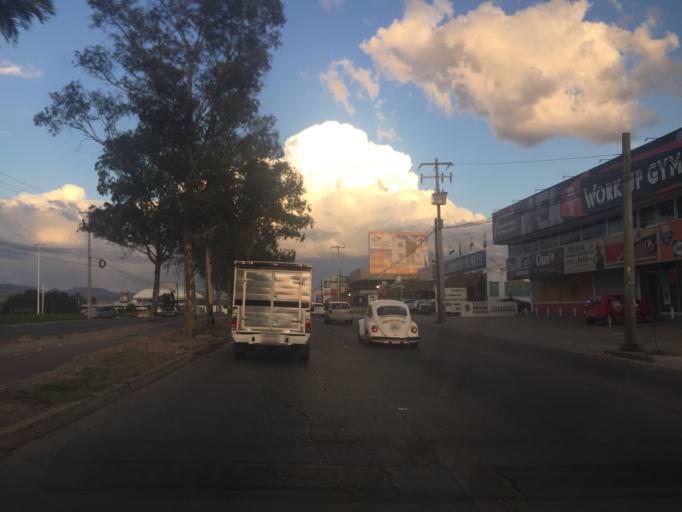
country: MX
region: Guanajuato
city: Leon
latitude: 21.0968
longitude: -101.6362
